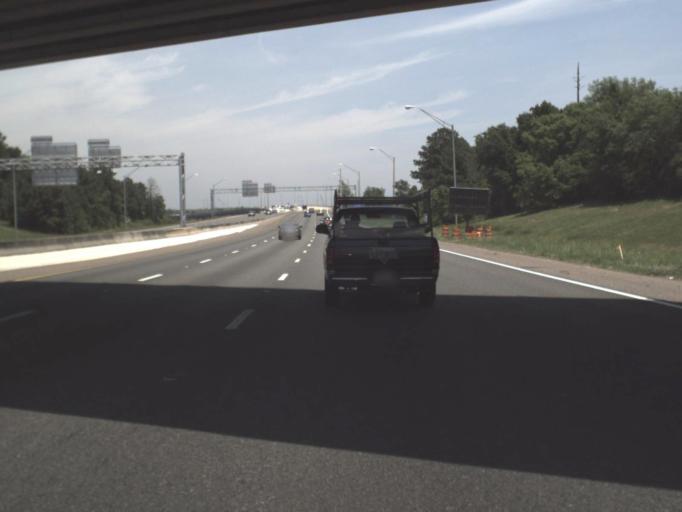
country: US
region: Florida
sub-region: Duval County
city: Jacksonville
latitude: 30.3618
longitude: -81.5532
